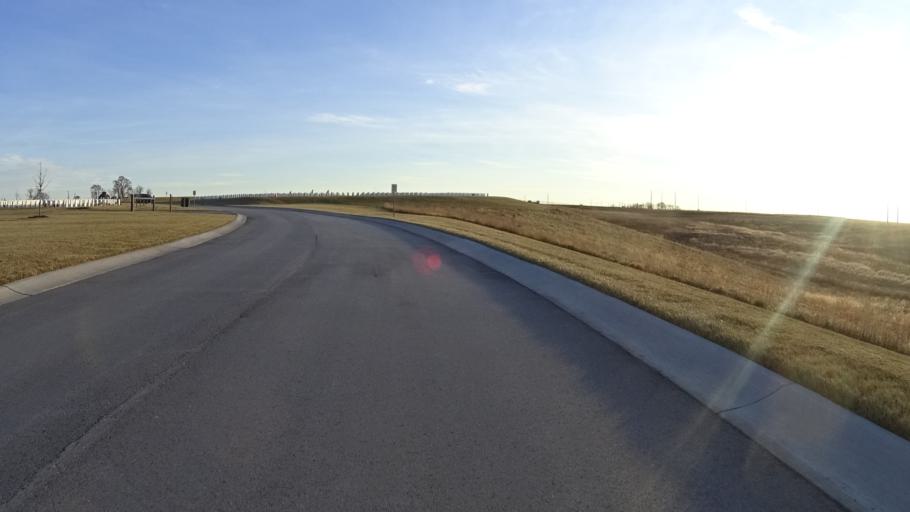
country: US
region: Nebraska
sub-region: Sarpy County
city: Chalco
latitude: 41.1361
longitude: -96.1343
